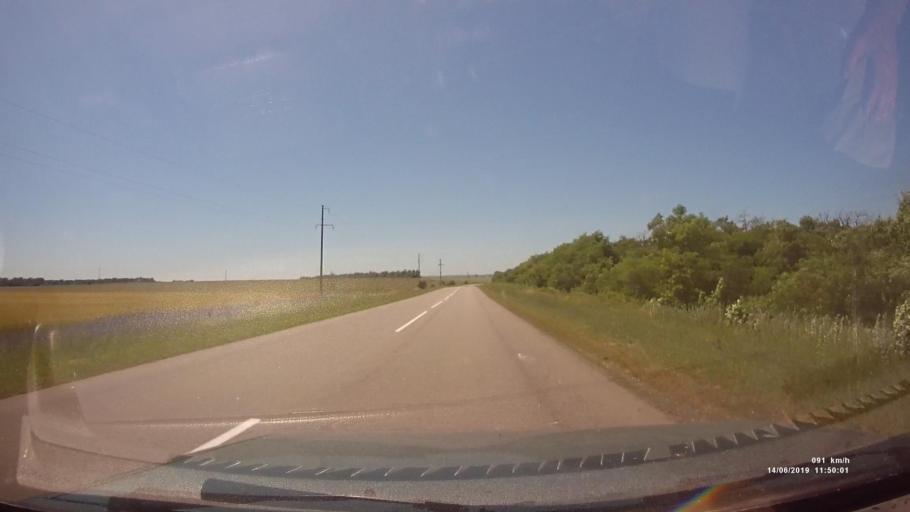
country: RU
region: Rostov
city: Kazanskaya
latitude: 49.8493
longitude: 41.2718
